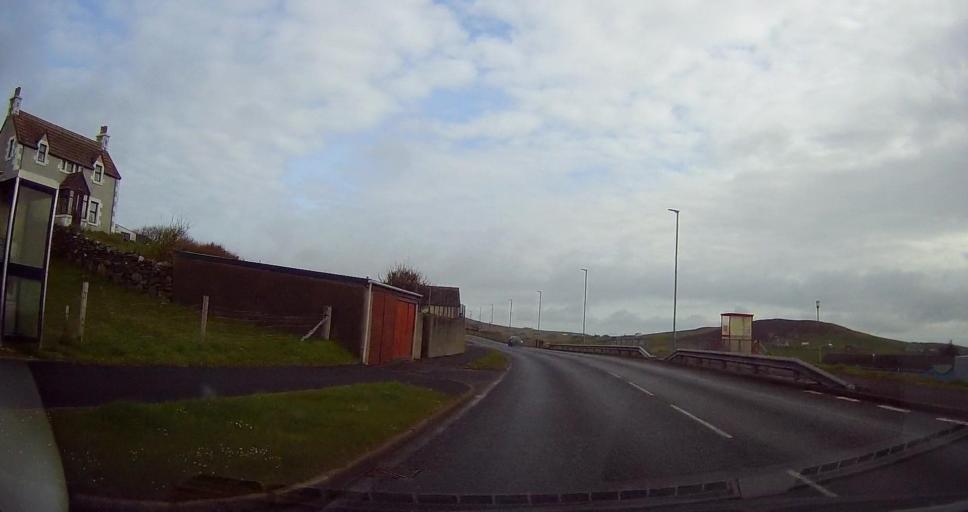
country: GB
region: Scotland
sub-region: Shetland Islands
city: Sandwick
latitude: 60.0454
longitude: -1.2283
